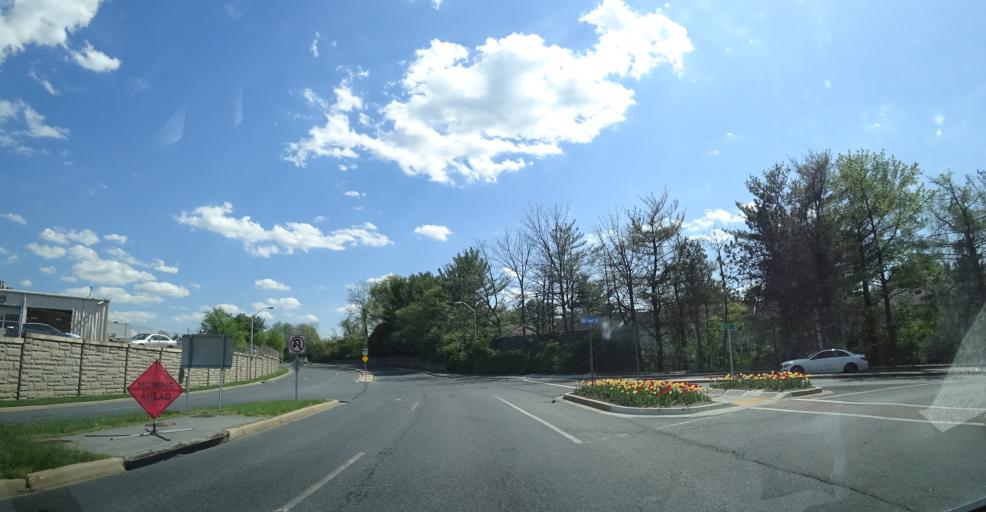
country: US
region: Maryland
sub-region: Montgomery County
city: Rockville
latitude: 39.0760
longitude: -77.1404
